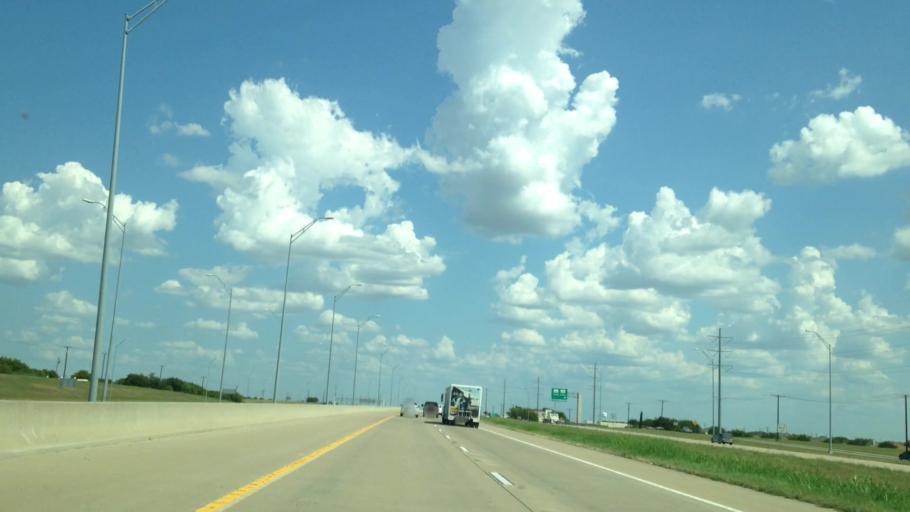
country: US
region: Texas
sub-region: Travis County
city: Pflugerville
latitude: 30.4823
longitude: -97.6107
